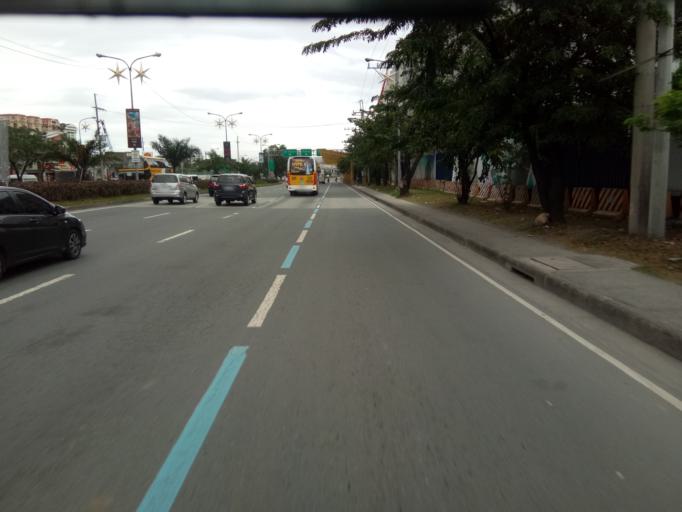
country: PH
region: Metro Manila
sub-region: Makati City
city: Makati City
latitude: 14.5241
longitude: 120.9904
